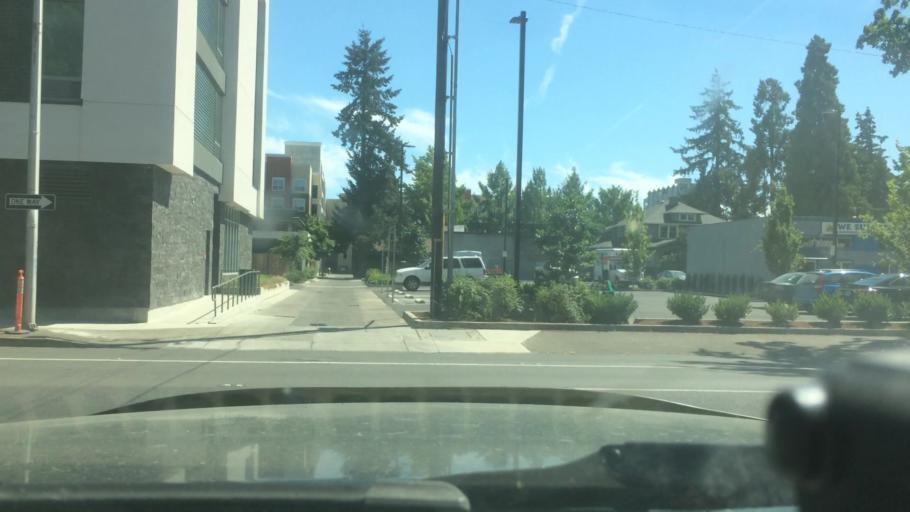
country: US
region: Oregon
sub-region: Lane County
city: Eugene
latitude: 44.0478
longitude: -123.0950
